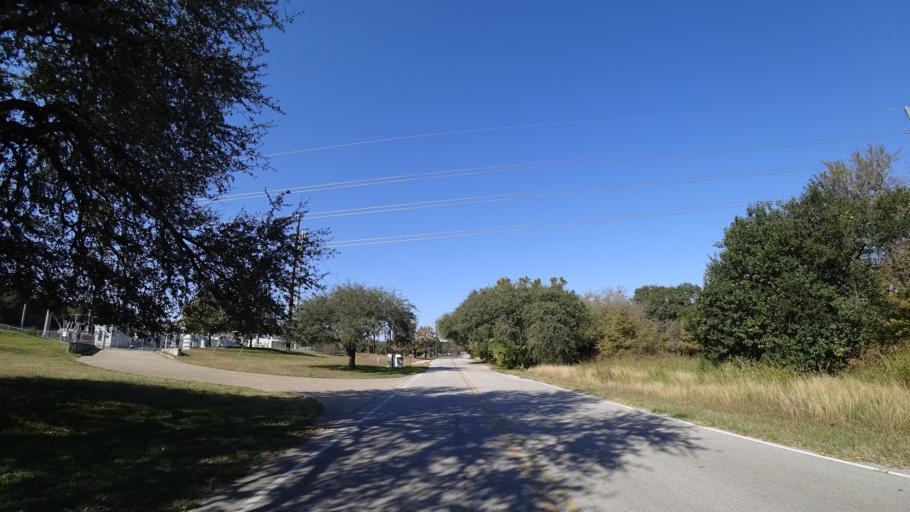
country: US
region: Texas
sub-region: Travis County
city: Barton Creek
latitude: 30.2340
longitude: -97.8583
